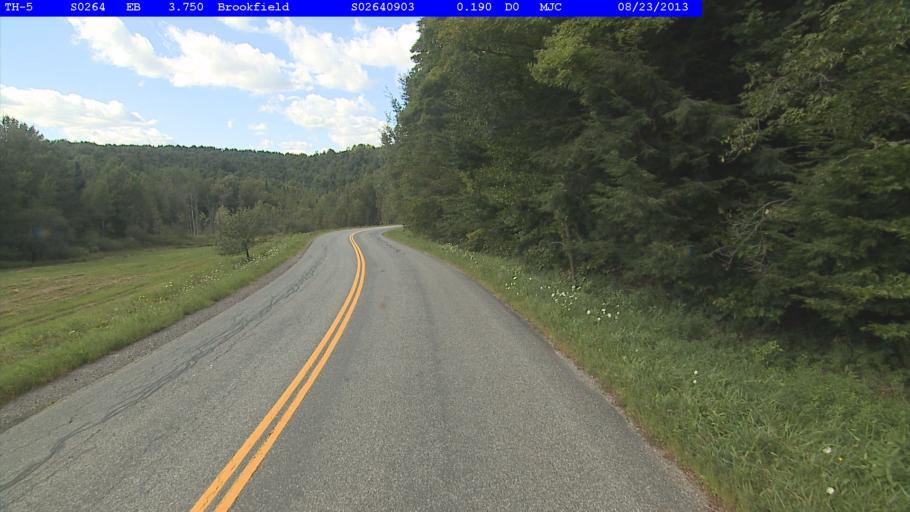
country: US
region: Vermont
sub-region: Orange County
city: Chelsea
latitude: 43.9692
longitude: -72.5131
